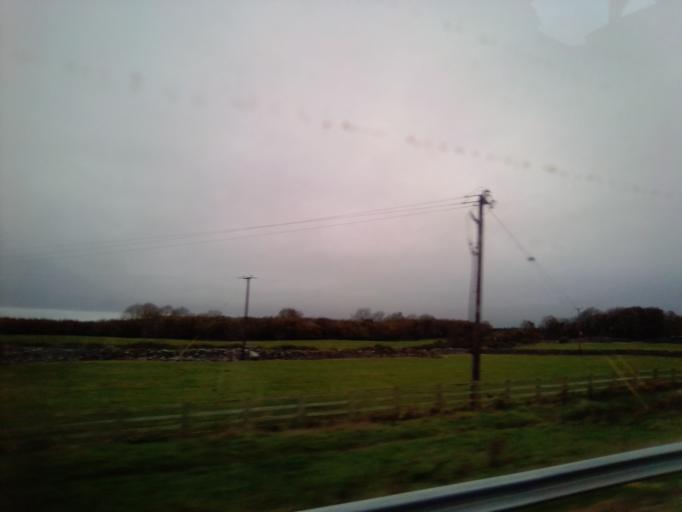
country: IE
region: Connaught
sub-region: County Galway
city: Athenry
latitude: 53.2778
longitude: -8.8018
